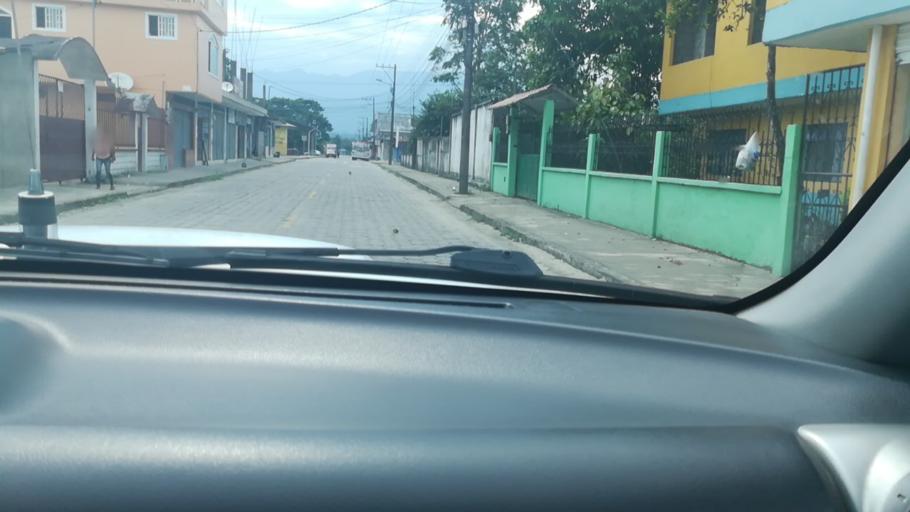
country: EC
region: Napo
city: Tena
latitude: -0.9875
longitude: -77.8195
